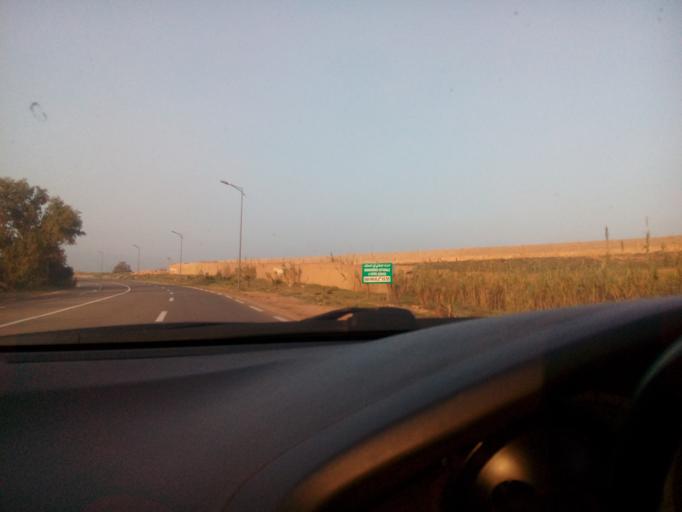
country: DZ
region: Oran
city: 'Ain el Turk
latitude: 35.7134
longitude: -0.8660
